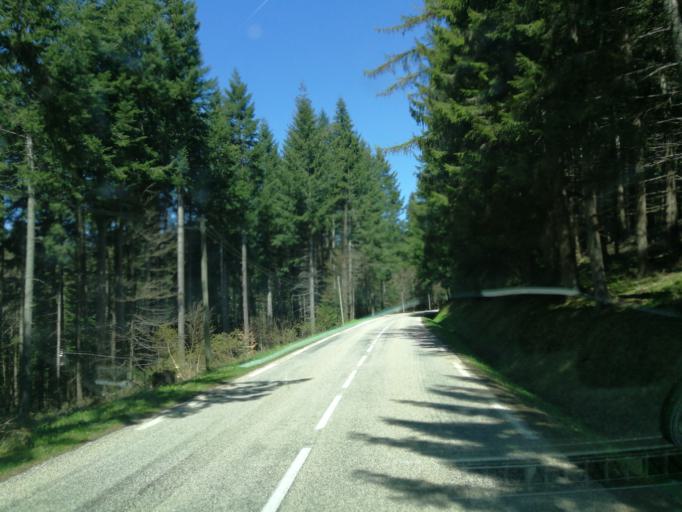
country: FR
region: Rhone-Alpes
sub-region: Departement de l'Ardeche
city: Saint-Agreve
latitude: 45.0240
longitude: 4.4071
